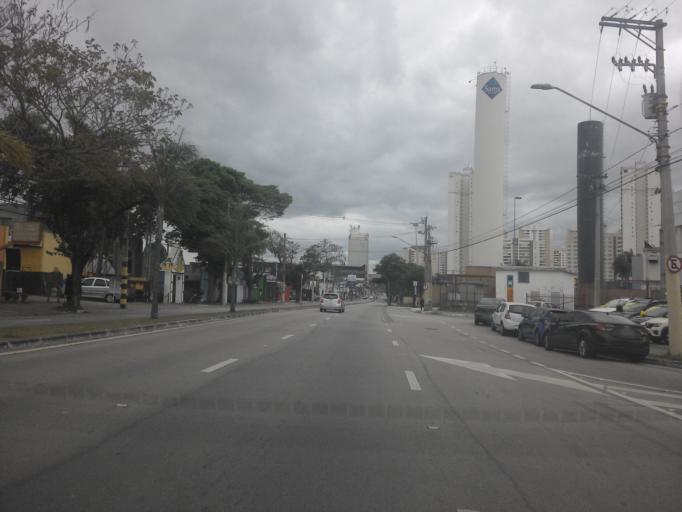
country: BR
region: Sao Paulo
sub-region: Sao Jose Dos Campos
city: Sao Jose dos Campos
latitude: -23.2289
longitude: -45.9124
